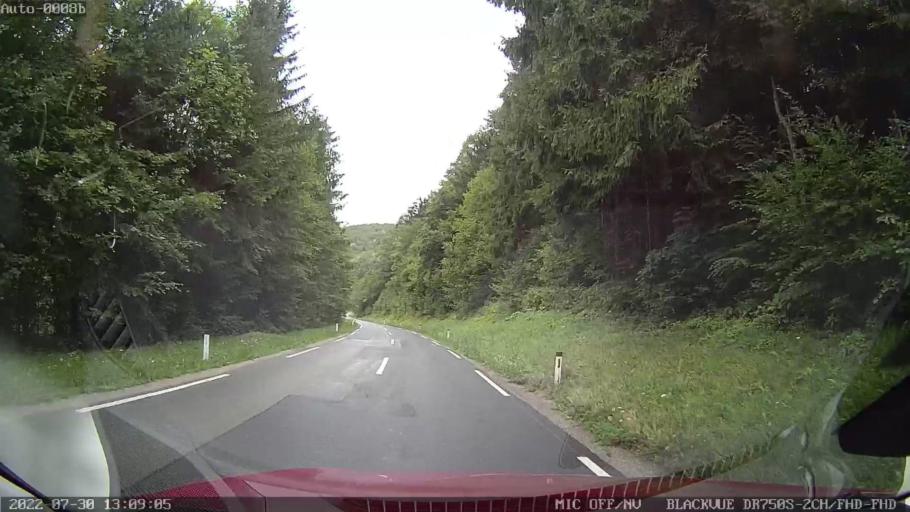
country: SI
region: Dolenjske Toplice
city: Dolenjske Toplice
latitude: 45.6846
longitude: 15.0986
